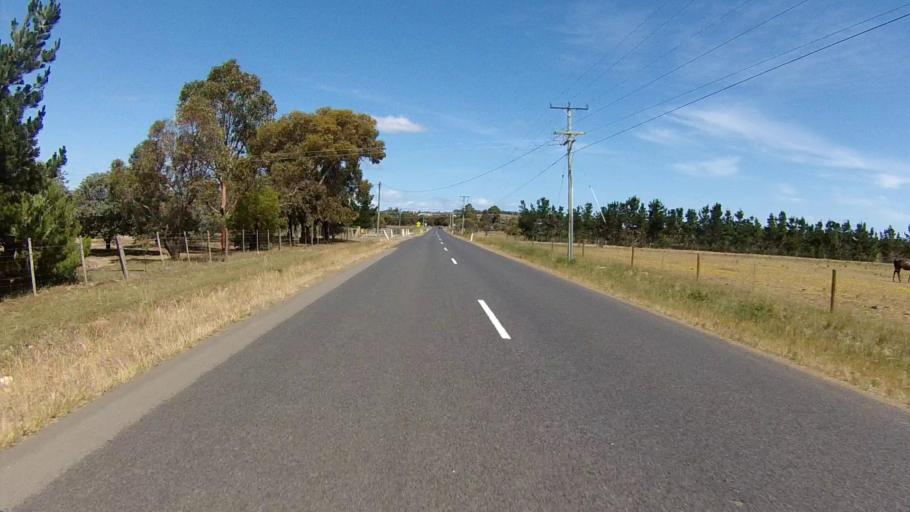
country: AU
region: Tasmania
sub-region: Sorell
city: Sorell
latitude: -42.7761
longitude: 147.5203
